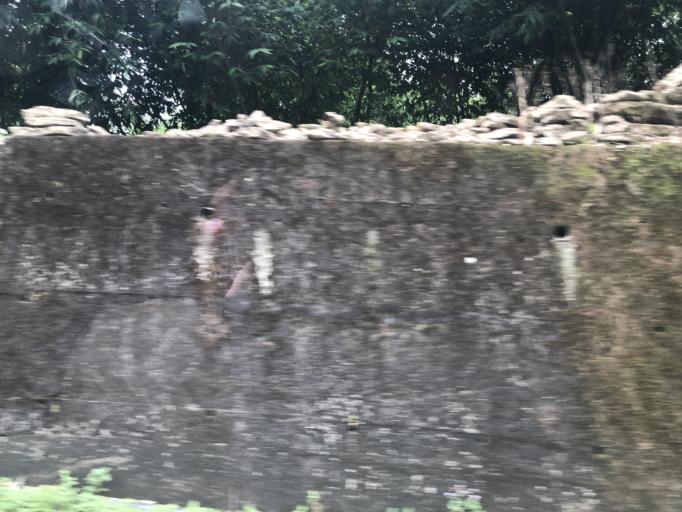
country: TW
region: Taiwan
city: Daxi
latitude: 24.8786
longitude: 121.4172
